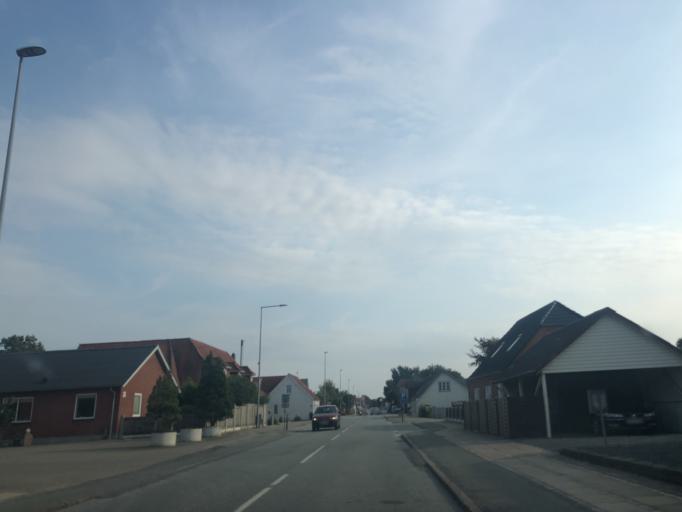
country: DK
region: Central Jutland
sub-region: Holstebro Kommune
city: Vinderup
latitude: 56.6168
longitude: 8.8799
